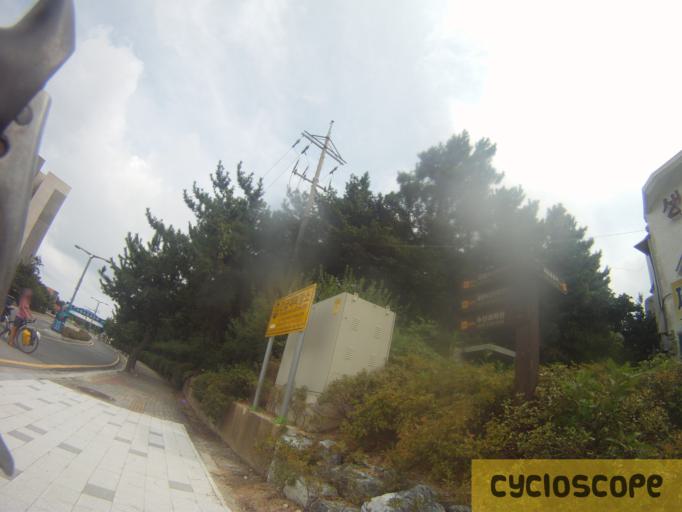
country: KR
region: Busan
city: Kijang
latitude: 35.1940
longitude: 129.2199
